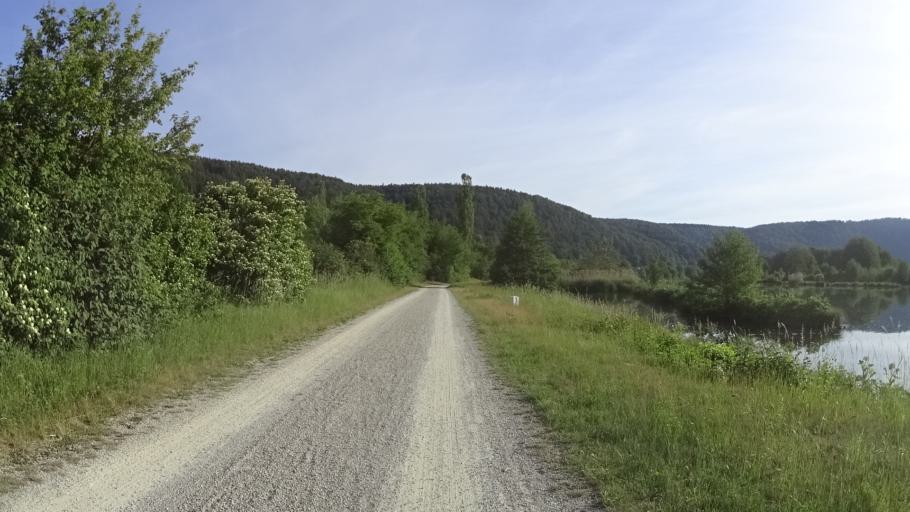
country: DE
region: Bavaria
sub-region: Lower Bavaria
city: Riedenburg
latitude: 48.9848
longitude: 11.6693
